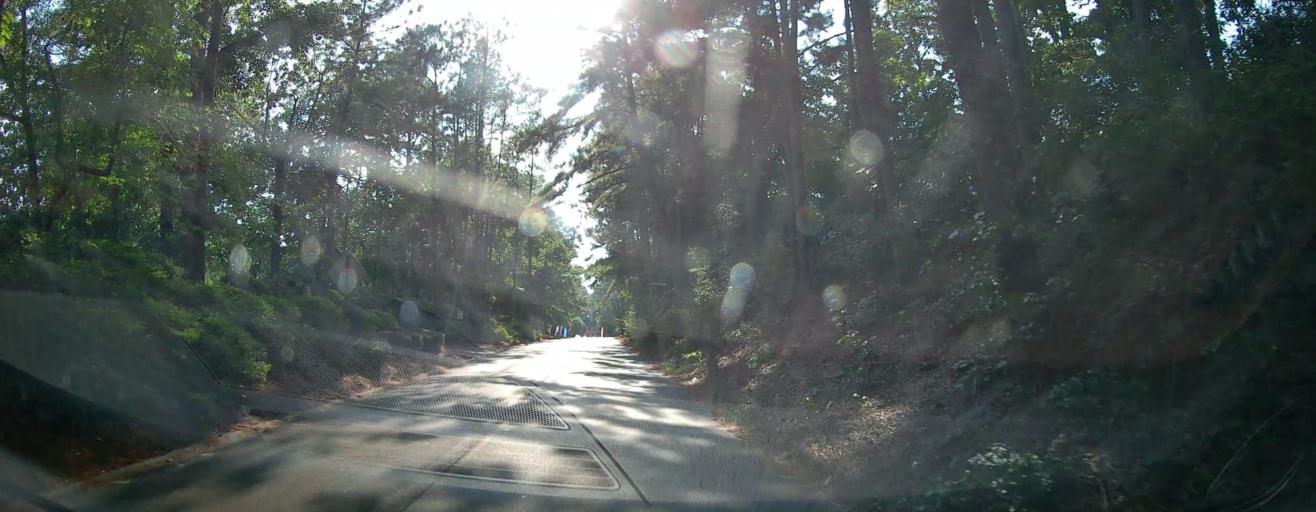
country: US
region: Georgia
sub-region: Houston County
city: Warner Robins
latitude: 32.5855
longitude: -83.6344
